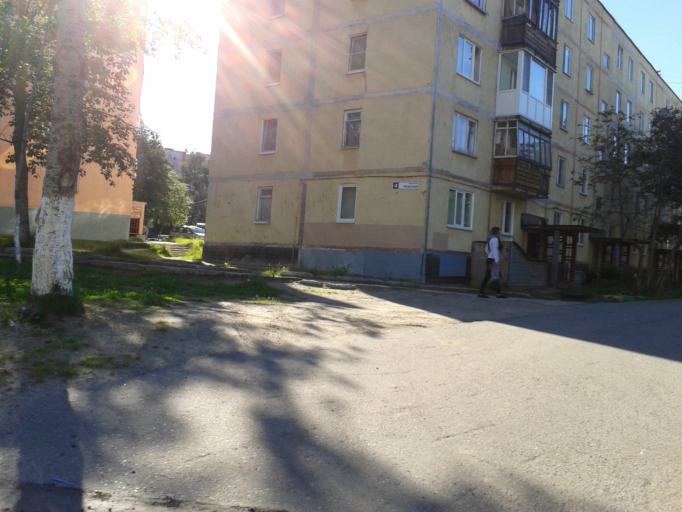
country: RU
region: Murmansk
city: Polyarnyye Zori
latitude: 67.3668
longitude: 32.5032
